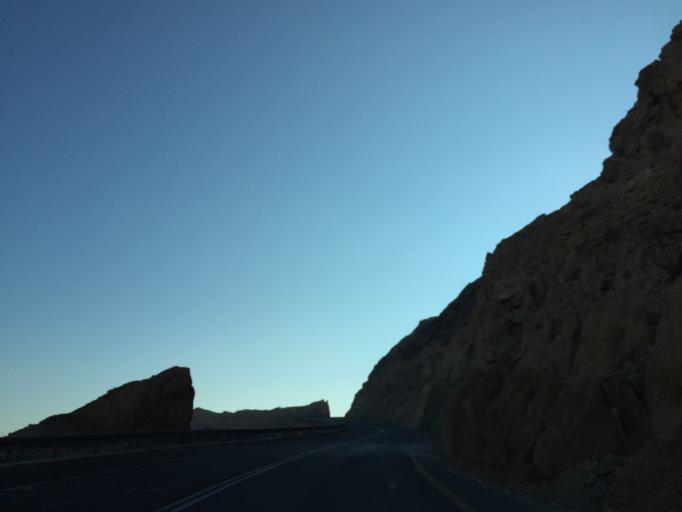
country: IL
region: Southern District
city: Mitzpe Ramon
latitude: 30.3208
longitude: 34.9608
